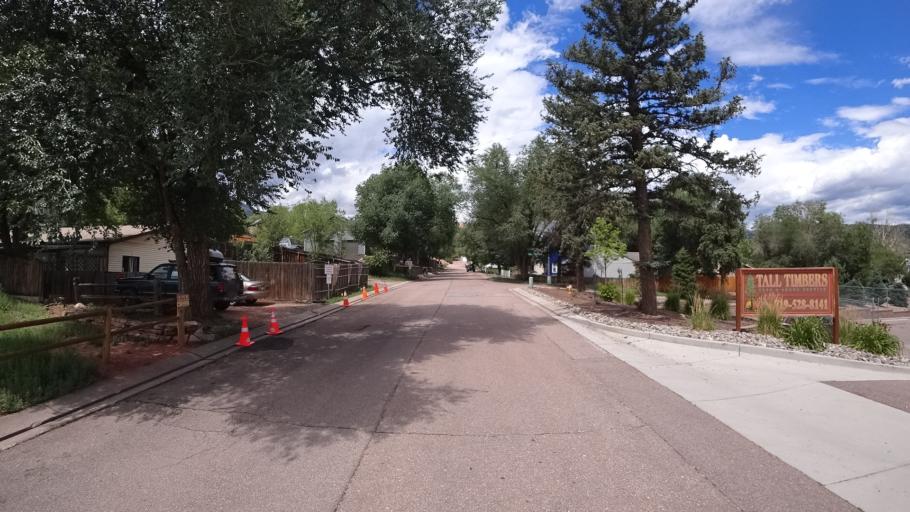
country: US
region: Colorado
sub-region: El Paso County
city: Manitou Springs
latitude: 38.8540
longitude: -104.8845
